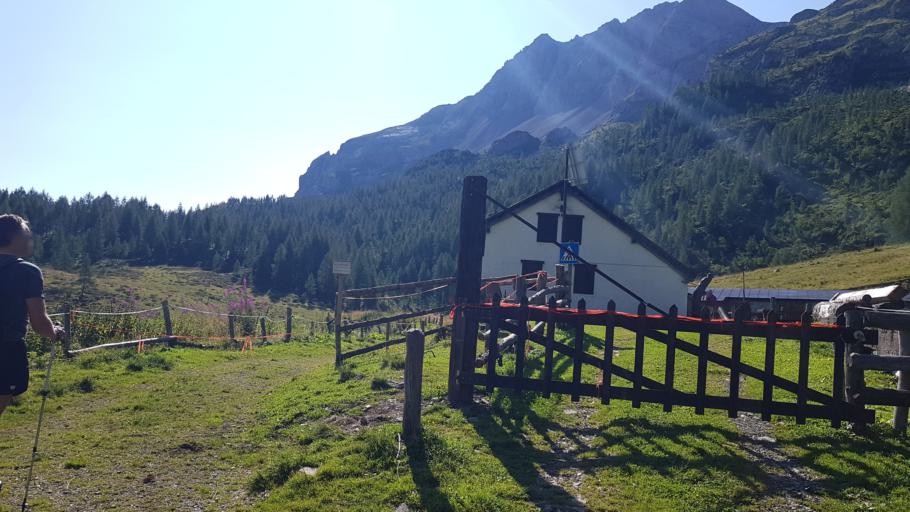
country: IT
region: Friuli Venezia Giulia
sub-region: Provincia di Udine
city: Vico
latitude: 46.4525
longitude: 12.6273
